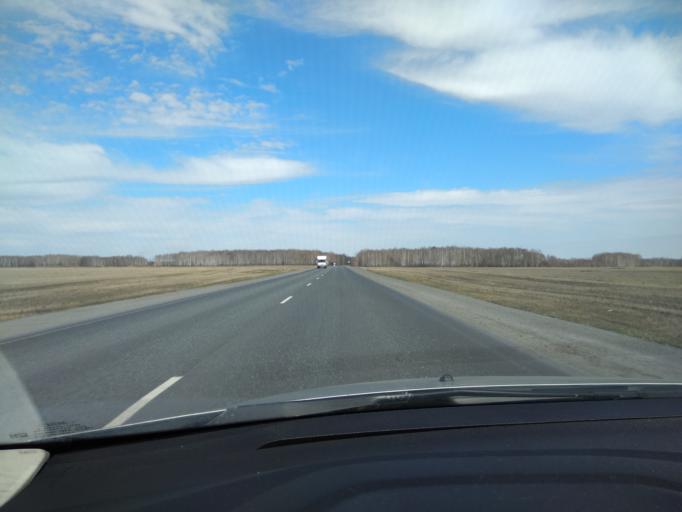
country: RU
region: Sverdlovsk
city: Pyshma
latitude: 56.9239
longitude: 63.1457
